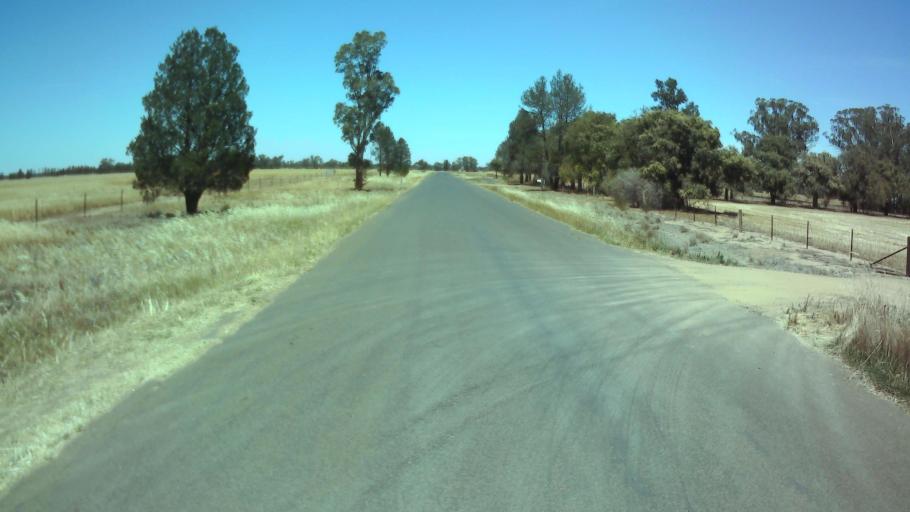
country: AU
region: New South Wales
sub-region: Weddin
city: Grenfell
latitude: -34.0310
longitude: 147.7906
